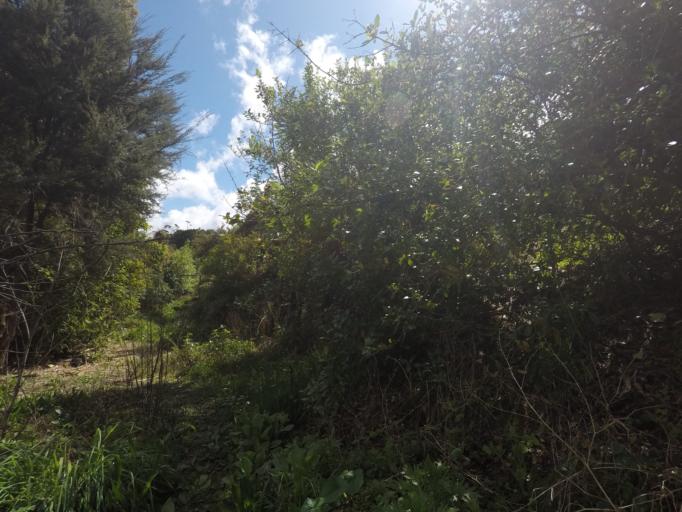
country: NZ
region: Auckland
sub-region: Auckland
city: Rosebank
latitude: -36.8811
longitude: 174.6698
